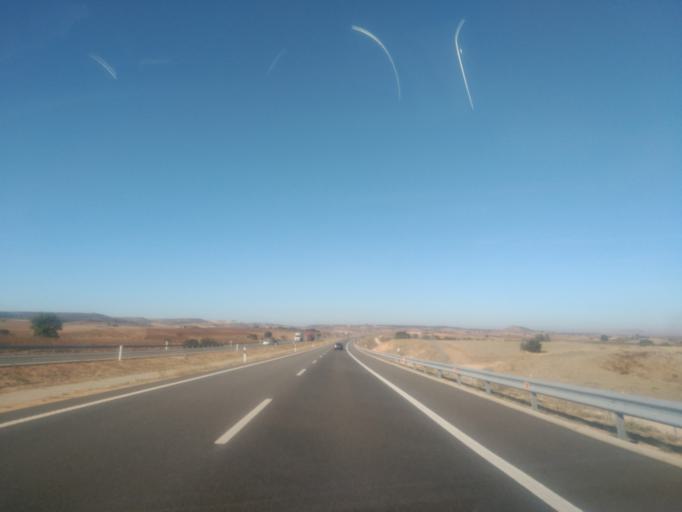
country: ES
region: Castille and Leon
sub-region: Provincia de Burgos
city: Castrillo de la Vega
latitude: 41.6336
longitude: -3.7613
